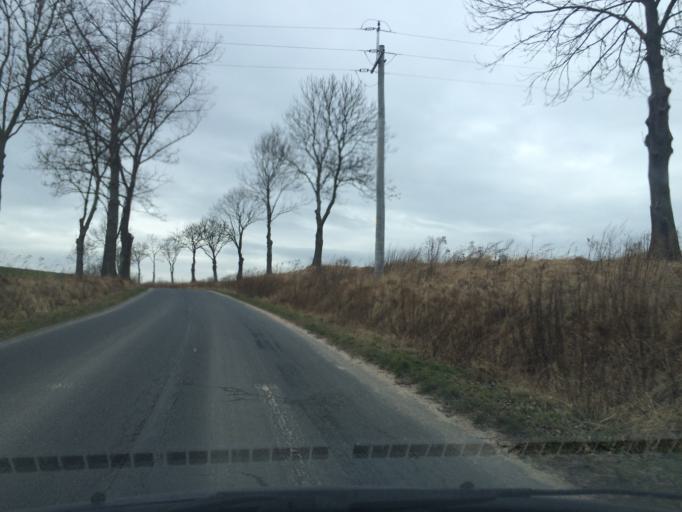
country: PL
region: Lower Silesian Voivodeship
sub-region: Powiat lwowecki
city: Lwowek Slaski
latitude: 51.1255
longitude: 15.4891
